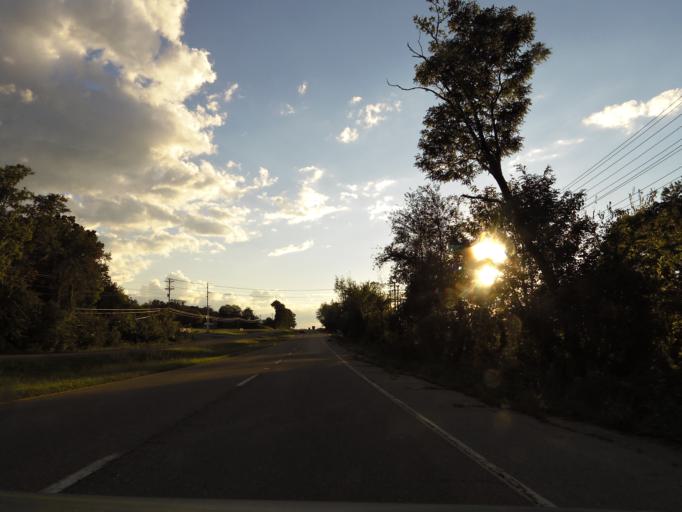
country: US
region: Tennessee
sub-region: Jefferson County
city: New Market
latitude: 36.0926
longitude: -83.5807
